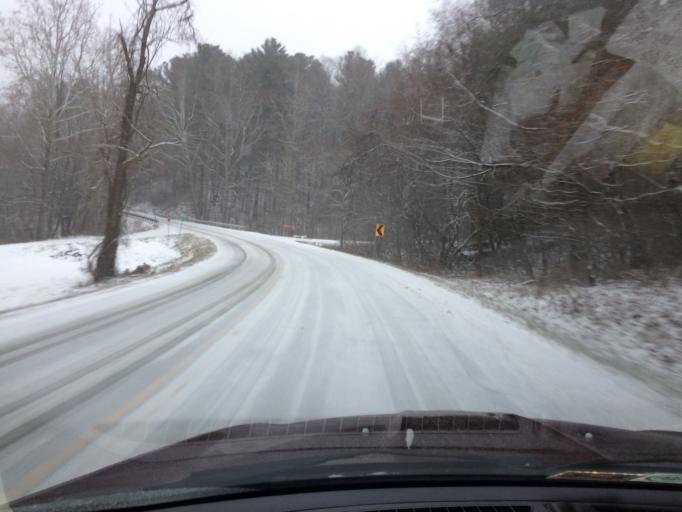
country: US
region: Virginia
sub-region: City of Buena Vista
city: Buena Vista
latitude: 37.7459
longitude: -79.2653
